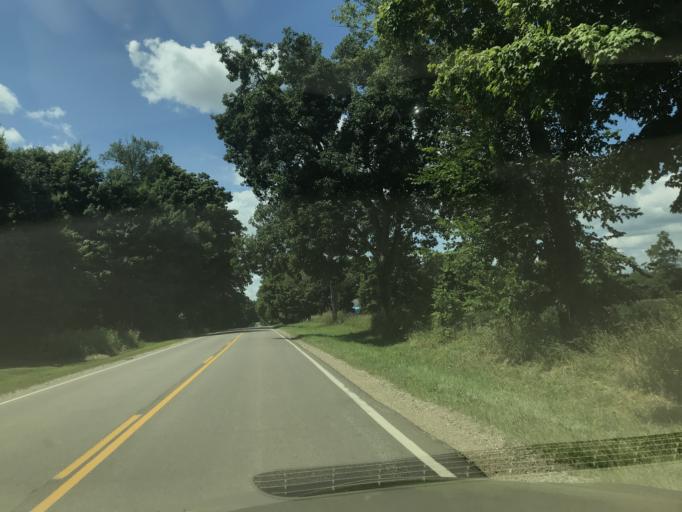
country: US
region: Michigan
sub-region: Ingham County
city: Leslie
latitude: 42.4512
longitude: -84.4807
